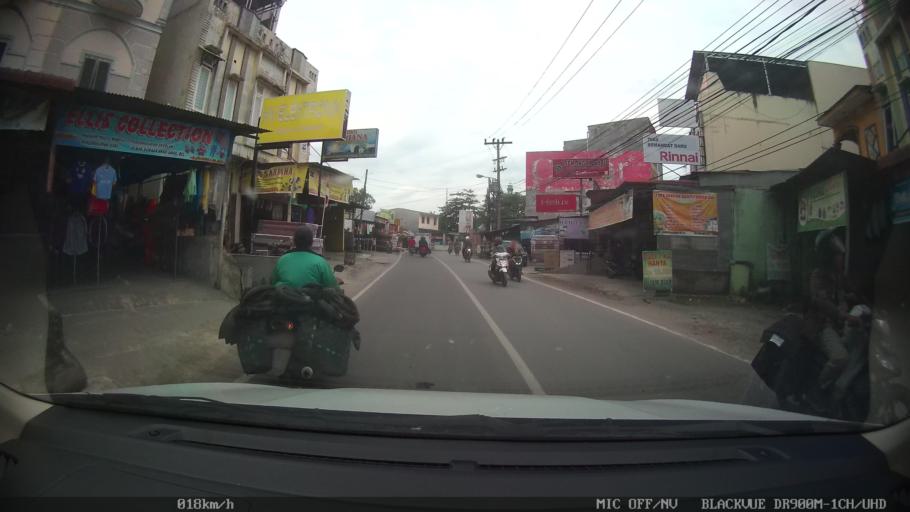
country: ID
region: North Sumatra
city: Sunggal
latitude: 3.6106
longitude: 98.6077
